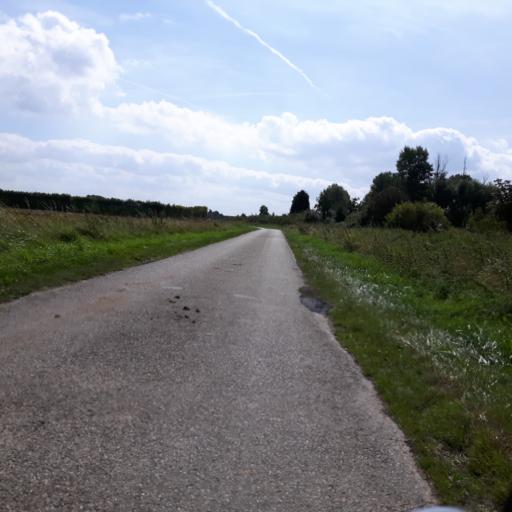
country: NL
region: Zeeland
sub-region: Gemeente Goes
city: Goes
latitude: 51.4682
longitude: 3.8968
